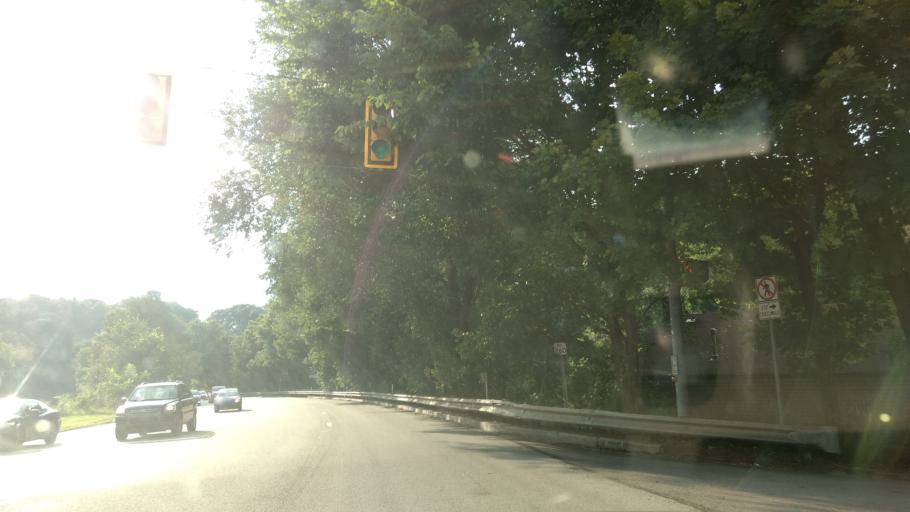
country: US
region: Pennsylvania
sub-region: Allegheny County
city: Glenshaw
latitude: 40.5299
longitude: -79.9529
